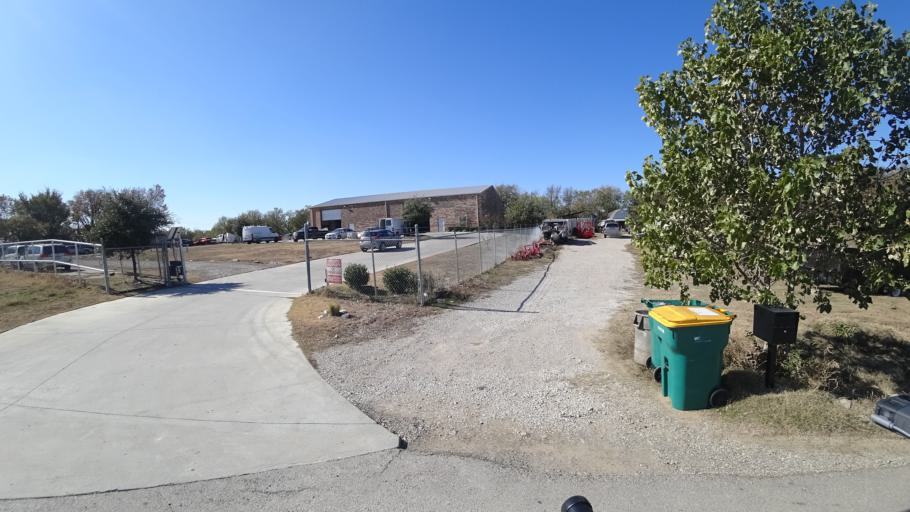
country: US
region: Texas
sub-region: Denton County
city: Lewisville
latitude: 33.0349
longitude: -96.9395
